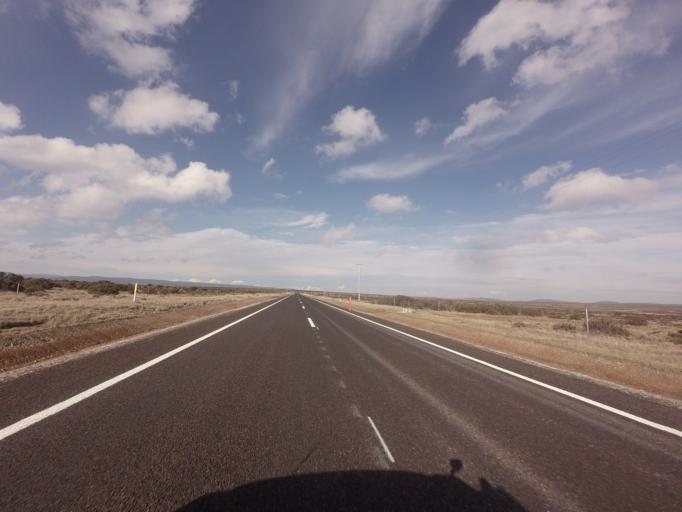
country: AU
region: Tasmania
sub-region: Meander Valley
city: Deloraine
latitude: -41.9102
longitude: 146.6804
